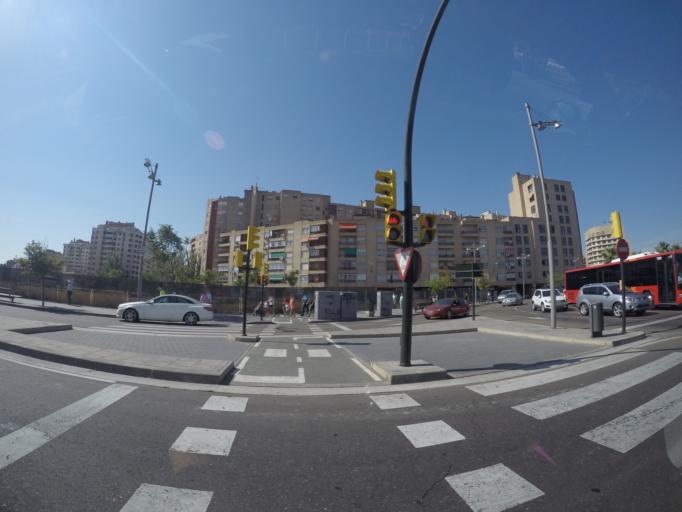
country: ES
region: Aragon
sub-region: Provincia de Zaragoza
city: Almozara
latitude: 41.6550
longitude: -0.8973
